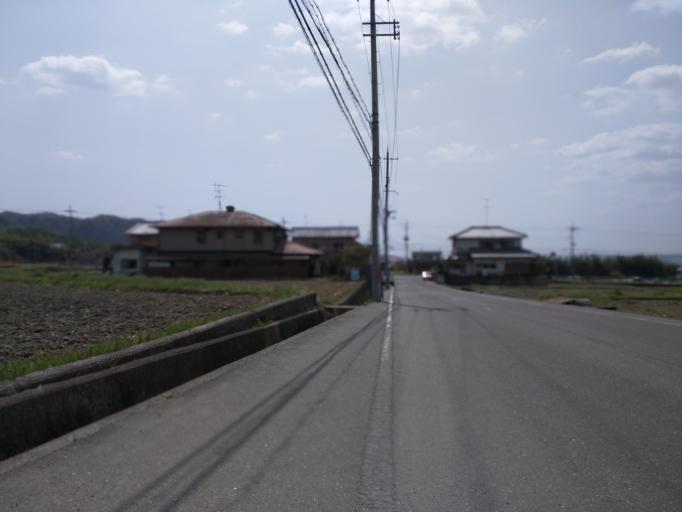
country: JP
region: Kyoto
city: Tanabe
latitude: 34.8020
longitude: 135.8142
